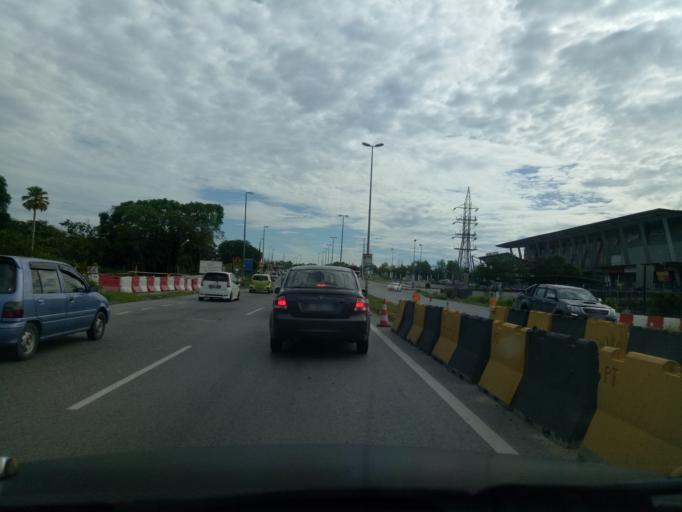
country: MY
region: Sarawak
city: Kuching
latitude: 1.4804
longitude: 110.3310
